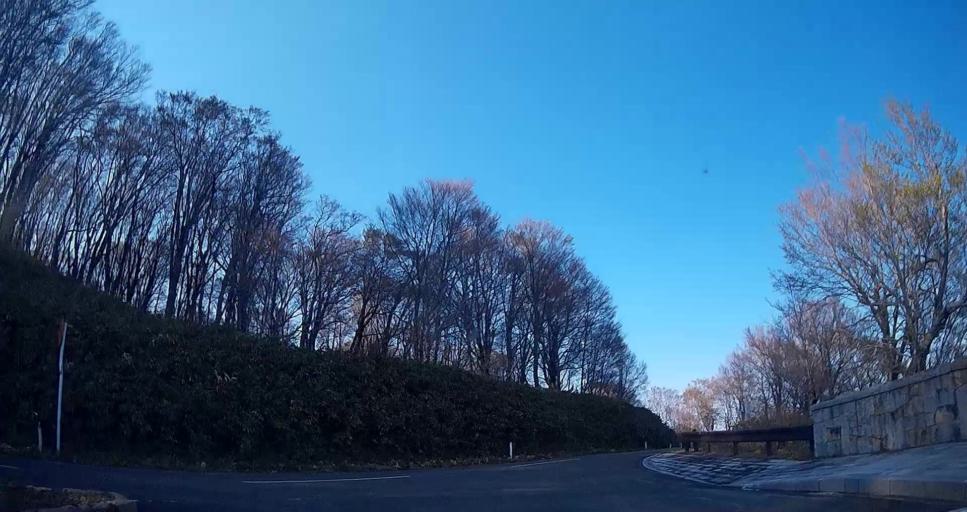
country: JP
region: Aomori
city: Mutsu
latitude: 41.3050
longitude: 141.1155
